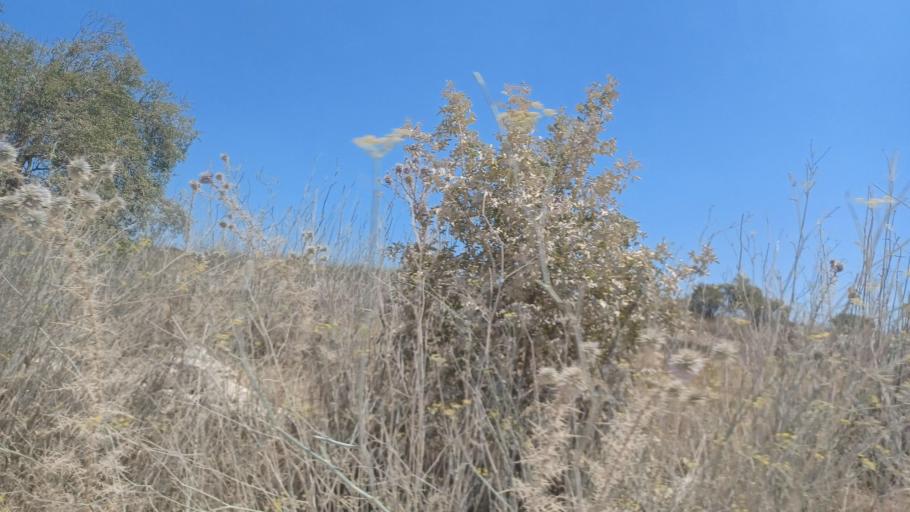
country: CY
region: Pafos
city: Pegeia
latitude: 34.9482
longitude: 32.4048
